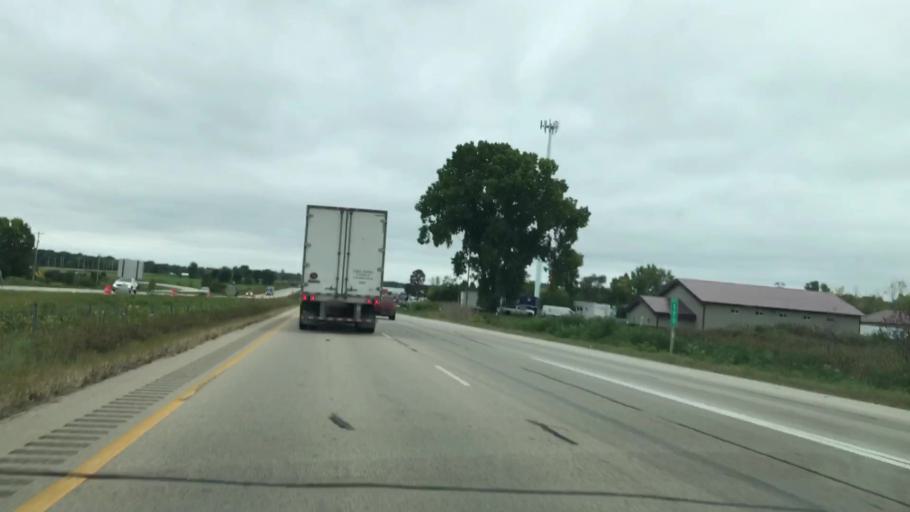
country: US
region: Wisconsin
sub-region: Brown County
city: Suamico
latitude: 44.6719
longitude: -88.0504
